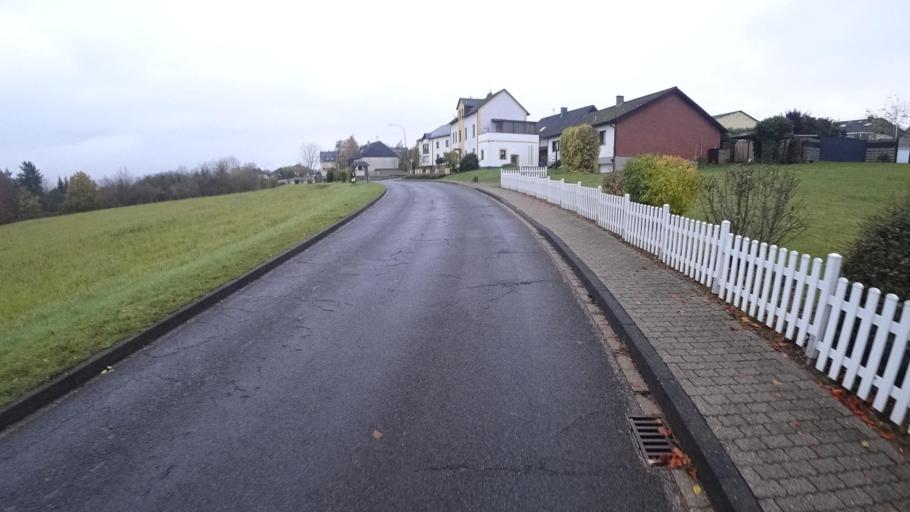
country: DE
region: Rheinland-Pfalz
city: Sankt Goar
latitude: 50.1507
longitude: 7.7032
